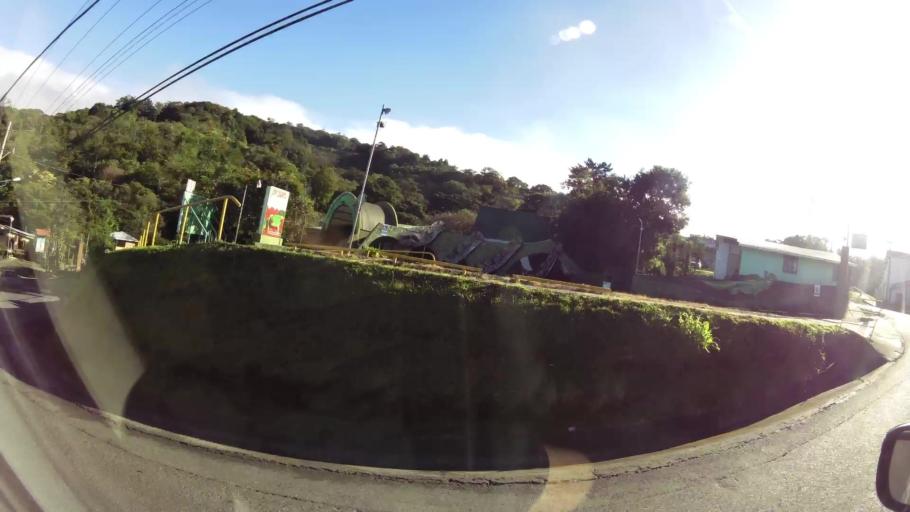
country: CR
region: Guanacaste
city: Juntas
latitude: 10.3159
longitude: -84.8228
